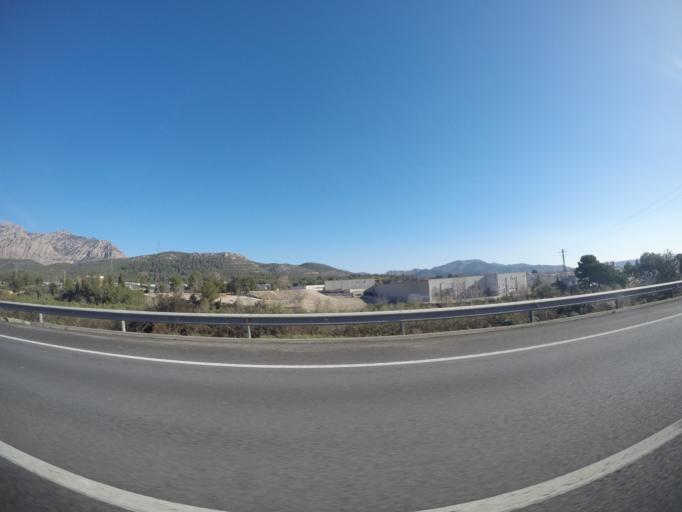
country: ES
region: Catalonia
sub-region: Provincia de Barcelona
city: Esparreguera
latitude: 41.5498
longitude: 1.8474
